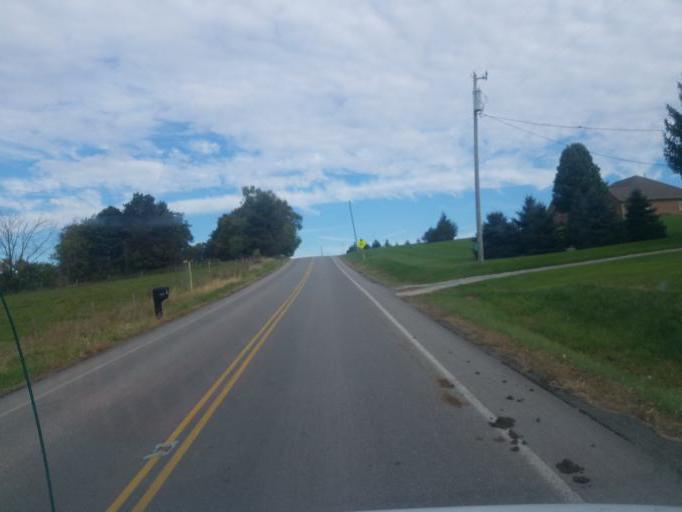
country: US
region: Ohio
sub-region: Wayne County
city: Dalton
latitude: 40.7115
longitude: -81.6974
